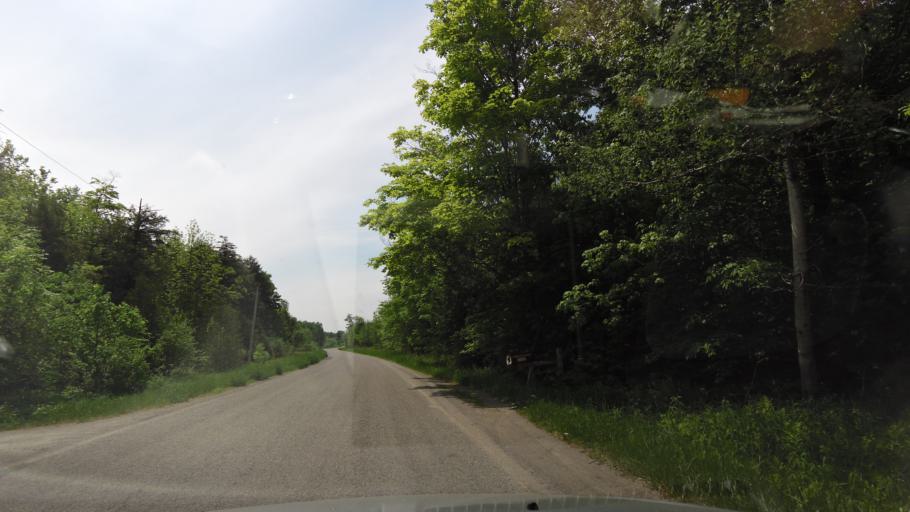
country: CA
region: Ontario
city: Cobourg
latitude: 43.9799
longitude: -78.4829
